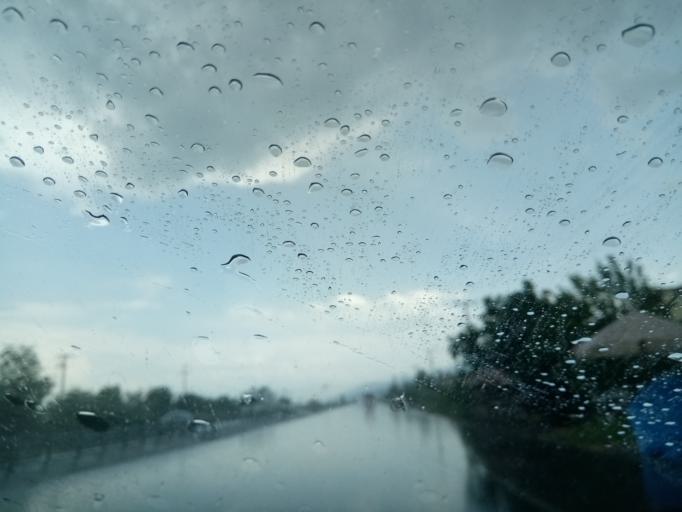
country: TR
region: Afyonkarahisar
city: Sultandagi
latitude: 38.4977
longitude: 31.2696
